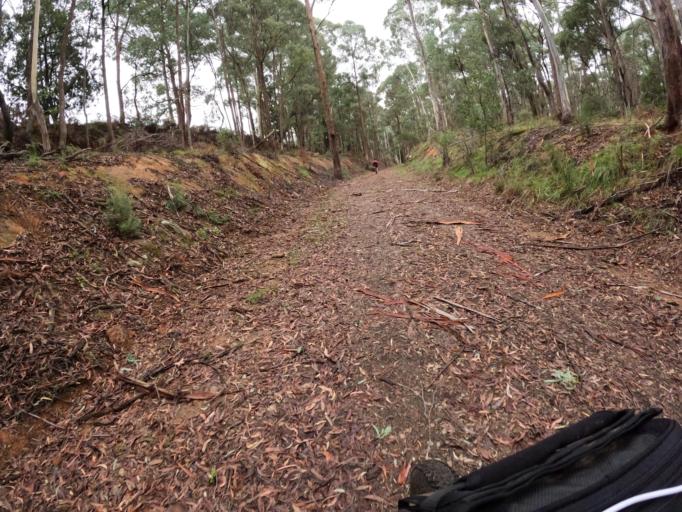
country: AU
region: New South Wales
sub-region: Greater Hume Shire
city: Holbrook
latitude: -36.1487
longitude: 147.4569
